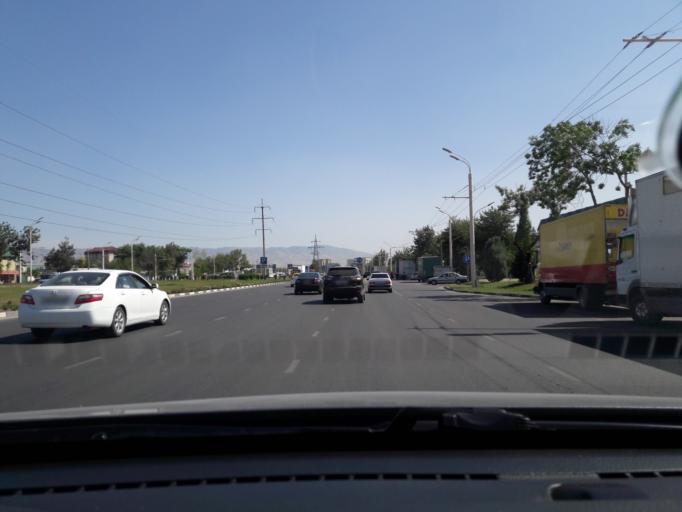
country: TJ
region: Dushanbe
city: Dushanbe
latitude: 38.5426
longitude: 68.7409
